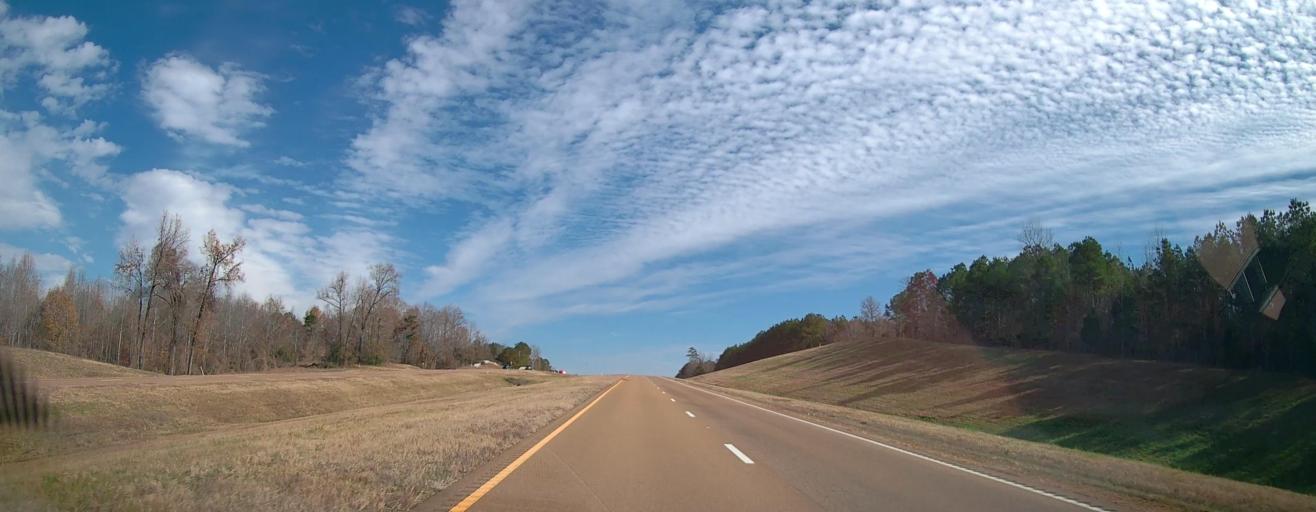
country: US
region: Mississippi
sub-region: Benton County
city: Ashland
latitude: 34.9499
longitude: -89.0872
